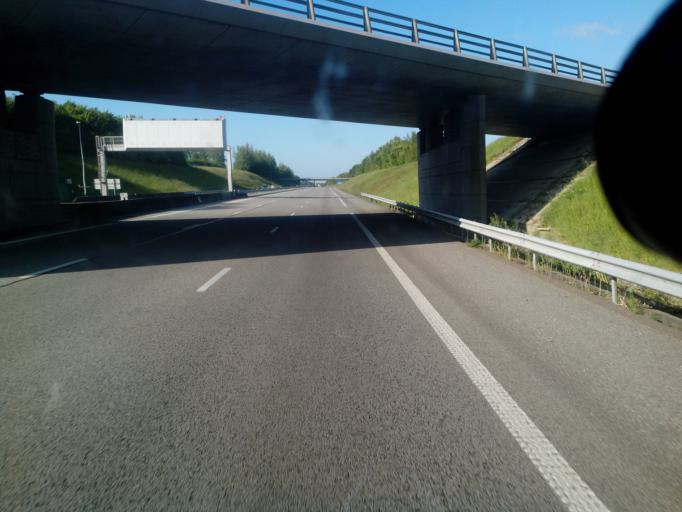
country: FR
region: Haute-Normandie
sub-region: Departement de la Seine-Maritime
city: Saint-Aubin-Routot
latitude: 49.5203
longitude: 0.3027
